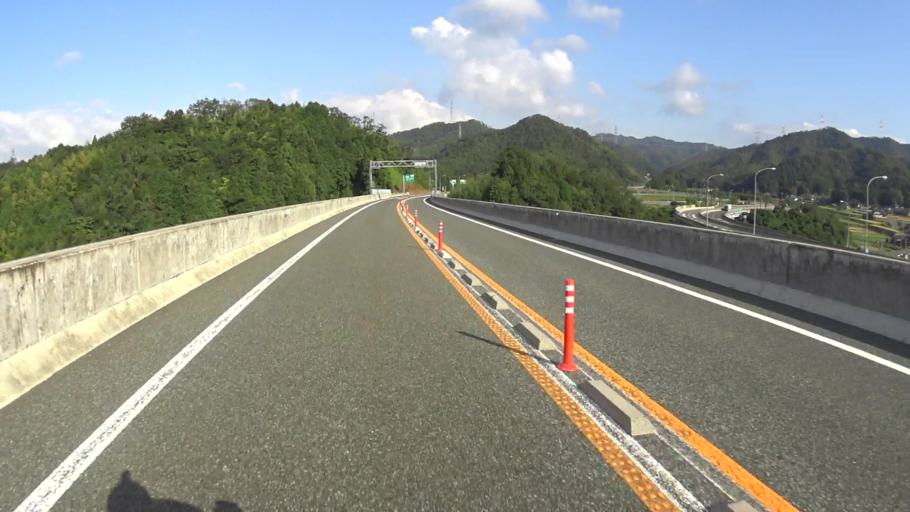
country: JP
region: Kyoto
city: Ayabe
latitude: 35.3501
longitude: 135.2913
